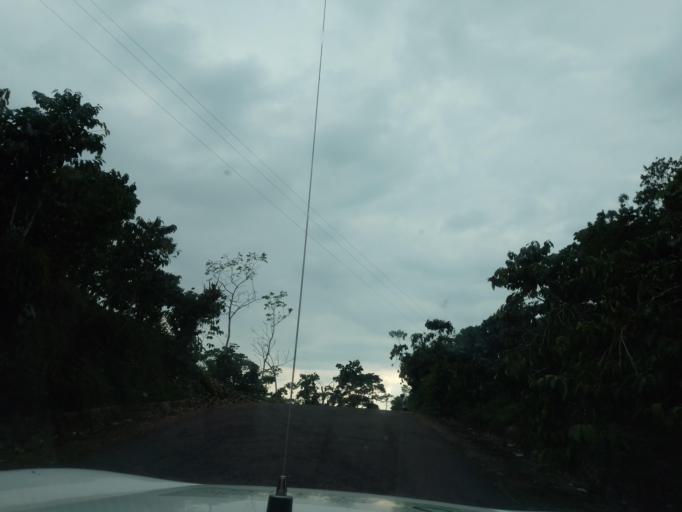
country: MX
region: Chiapas
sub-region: Union Juarez
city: Santo Domingo
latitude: 15.0490
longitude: -92.1196
